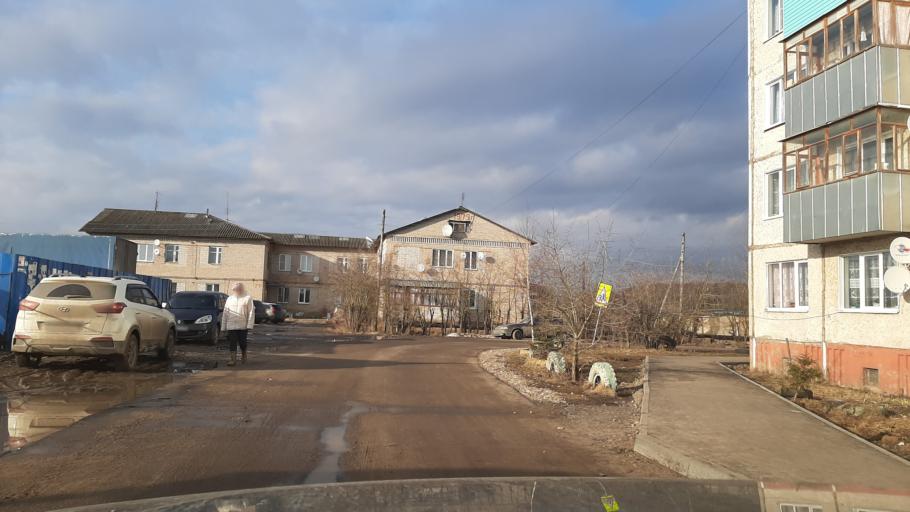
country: RU
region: Ivanovo
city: Novo-Talitsy
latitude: 56.9228
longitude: 40.7347
